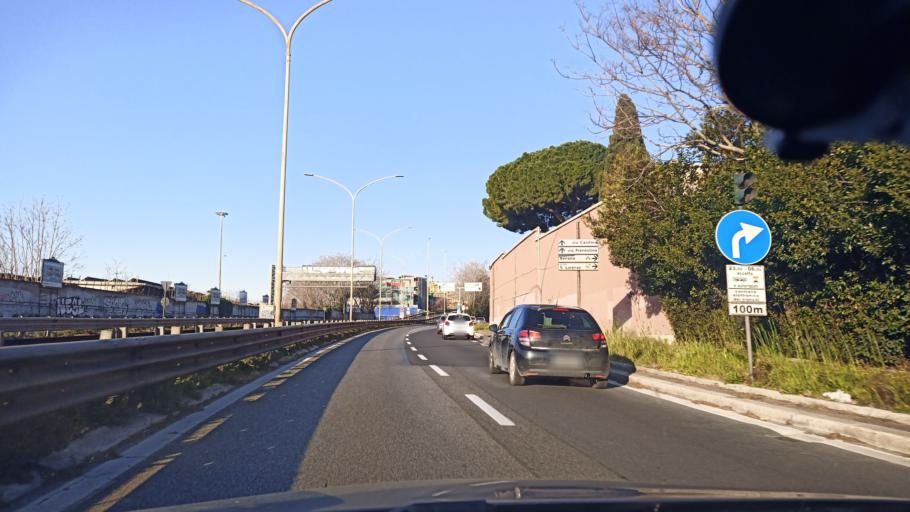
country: IT
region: Latium
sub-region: Citta metropolitana di Roma Capitale
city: Rome
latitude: 41.8978
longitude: 12.5254
